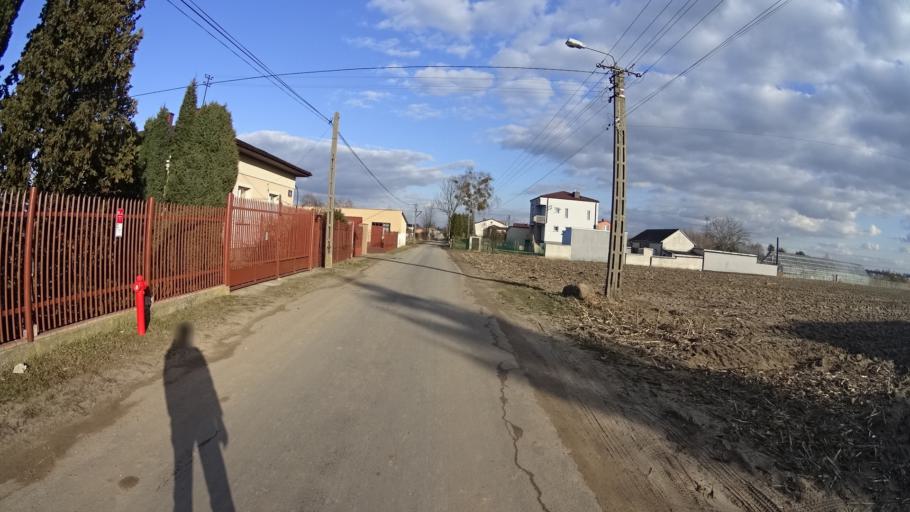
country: PL
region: Masovian Voivodeship
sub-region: Powiat warszawski zachodni
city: Hornowek
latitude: 52.2623
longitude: 20.8018
